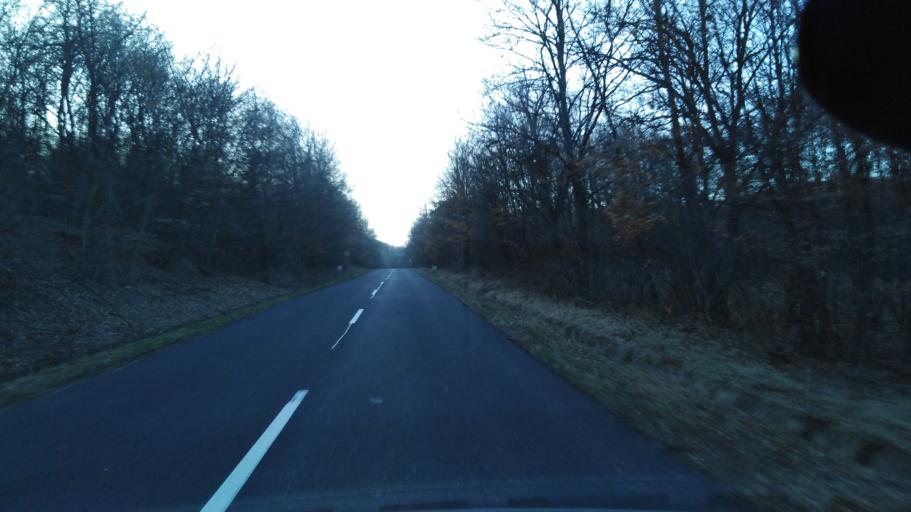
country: HU
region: Nograd
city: Salgotarjan
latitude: 48.0662
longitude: 19.8240
